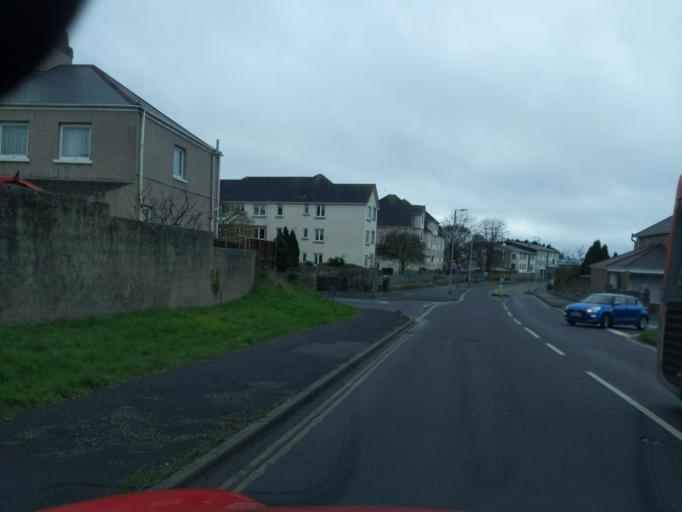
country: GB
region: England
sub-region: Plymouth
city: Plymstock
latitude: 50.3604
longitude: -4.0857
